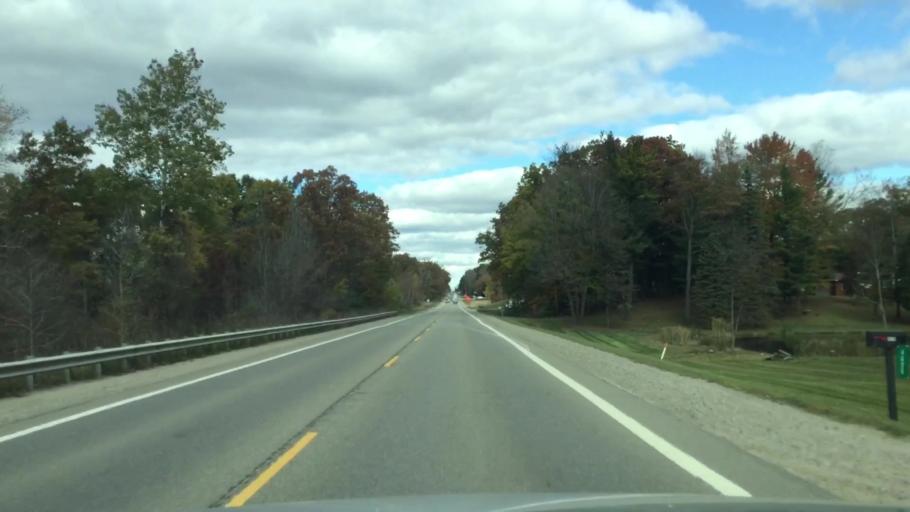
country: US
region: Michigan
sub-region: Lapeer County
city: Barnes Lake-Millers Lake
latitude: 43.1640
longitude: -83.3118
